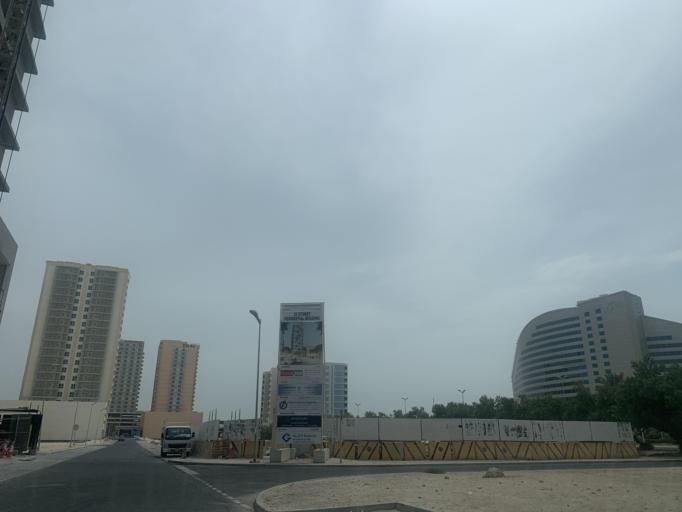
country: BH
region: Muharraq
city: Al Hadd
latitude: 26.2909
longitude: 50.6624
